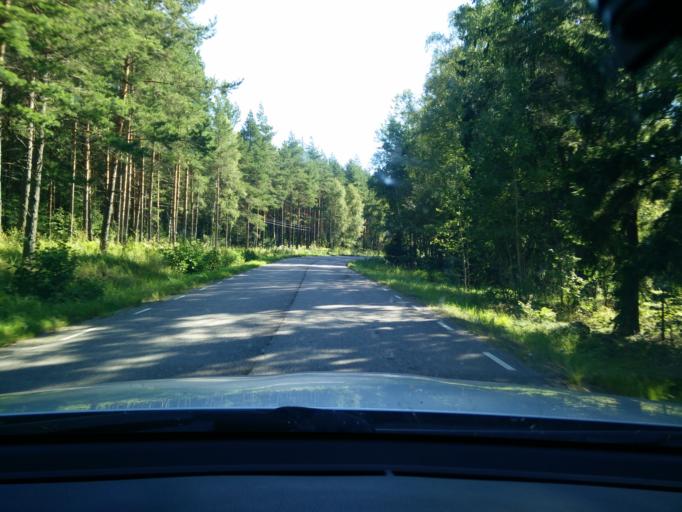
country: SE
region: Stockholm
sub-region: Taby Kommun
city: Taby
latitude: 59.4684
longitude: 18.1714
